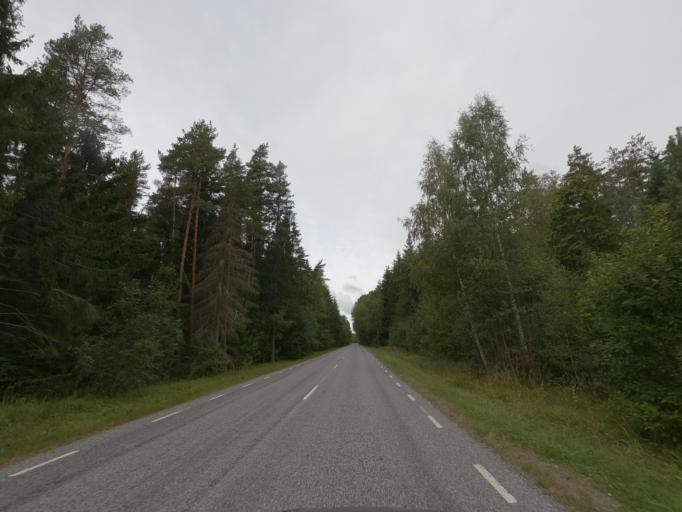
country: EE
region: Raplamaa
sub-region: Rapla vald
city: Rapla
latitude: 59.0074
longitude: 24.6144
